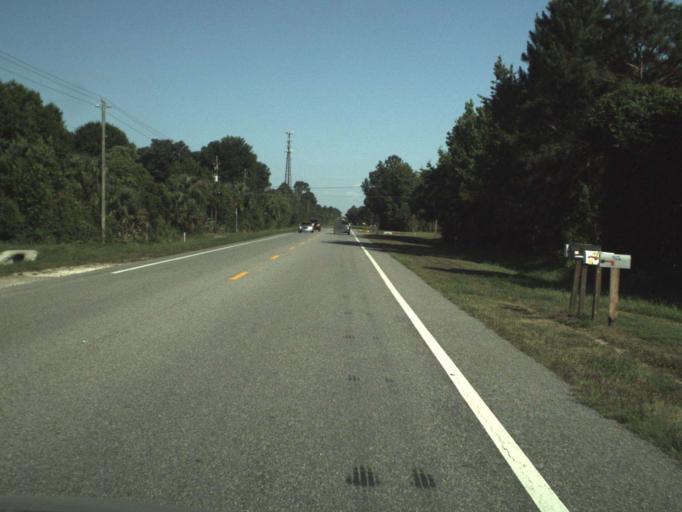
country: US
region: Florida
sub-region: Seminole County
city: Geneva
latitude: 28.7560
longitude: -81.1404
